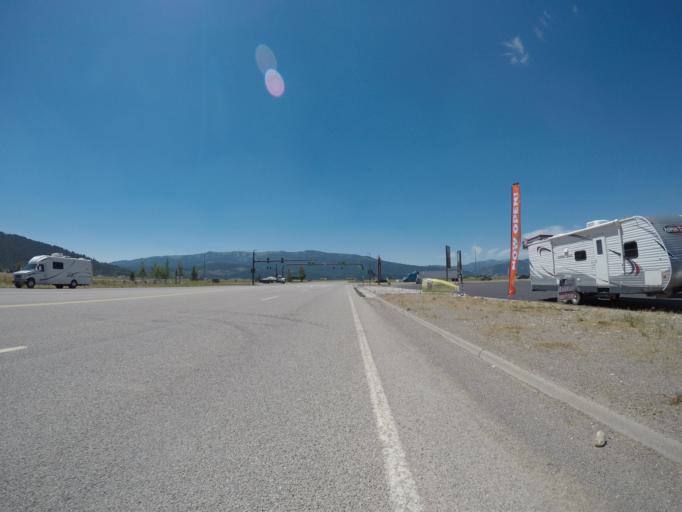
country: US
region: Wyoming
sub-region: Teton County
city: Hoback
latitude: 43.1726
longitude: -111.0172
